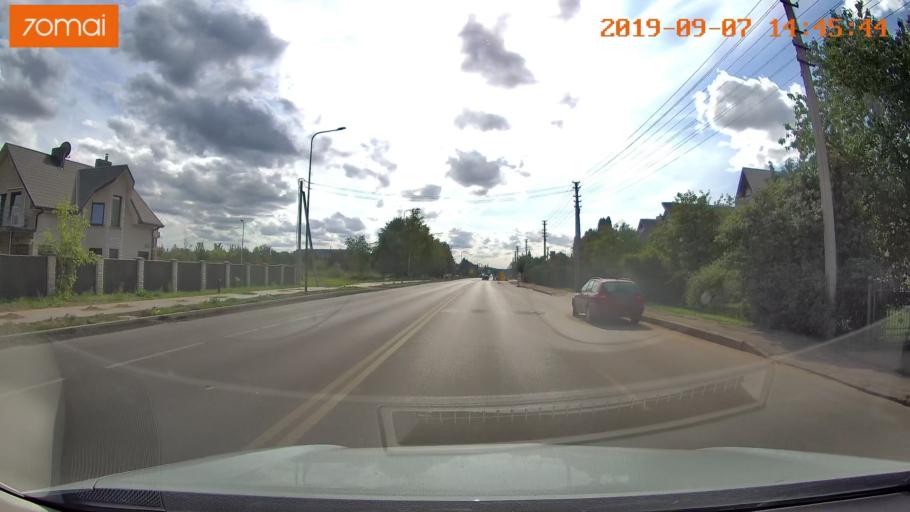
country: LT
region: Kauno apskritis
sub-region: Kaunas
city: Silainiai
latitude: 54.9309
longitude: 23.9087
